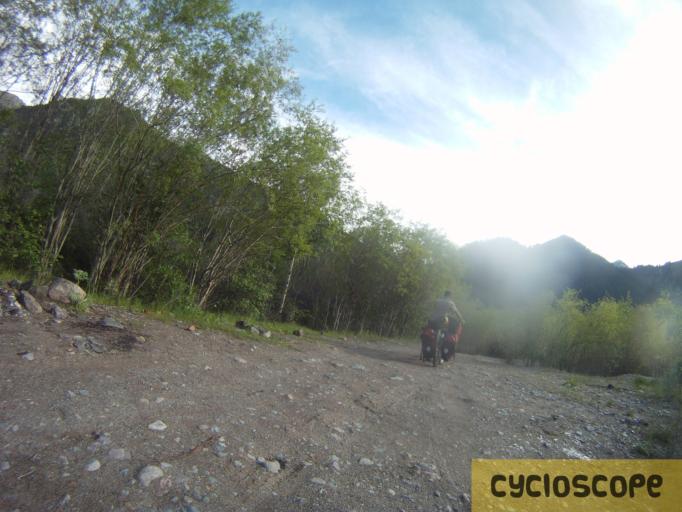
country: KZ
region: Almaty Oblysy
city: Esik
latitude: 43.2536
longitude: 77.4792
